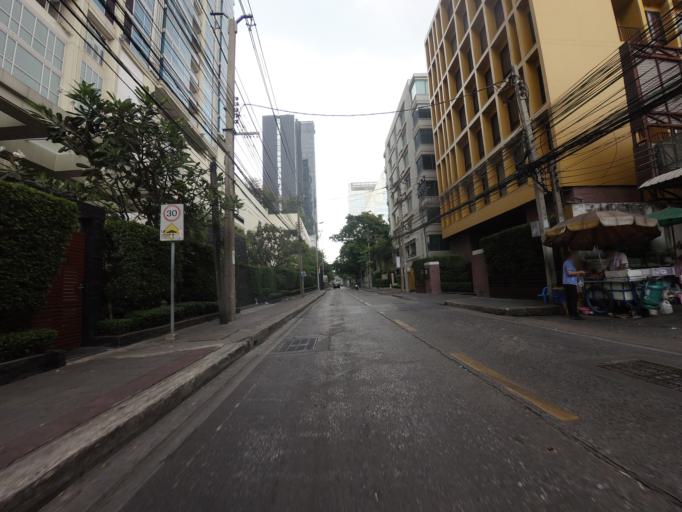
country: TH
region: Bangkok
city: Ratchathewi
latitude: 13.7412
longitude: 100.5491
